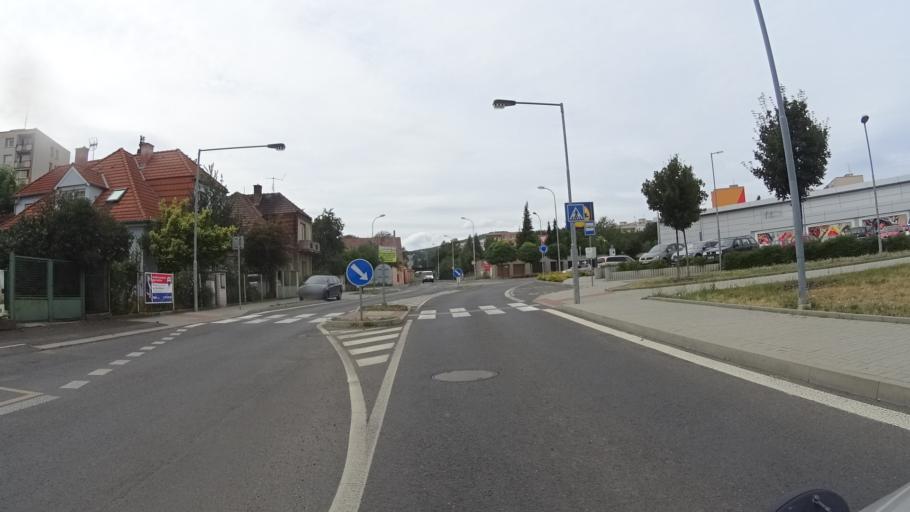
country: CZ
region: Ustecky
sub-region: Okres Litomerice
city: Litomerice
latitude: 50.5395
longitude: 14.1212
